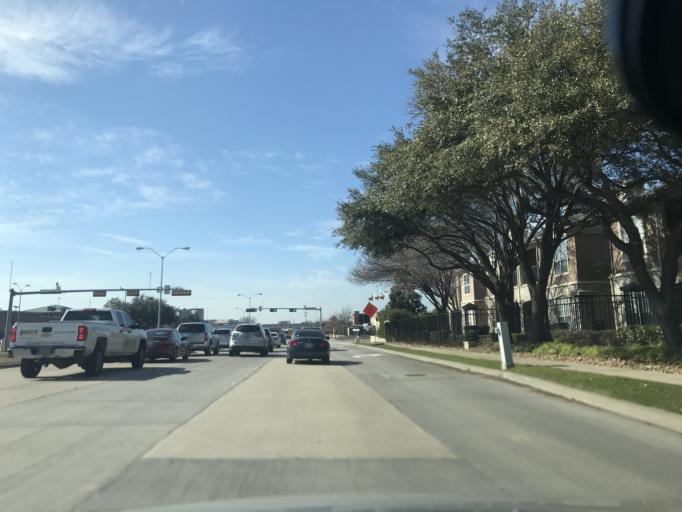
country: US
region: Texas
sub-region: Denton County
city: The Colony
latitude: 33.0454
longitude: -96.8260
